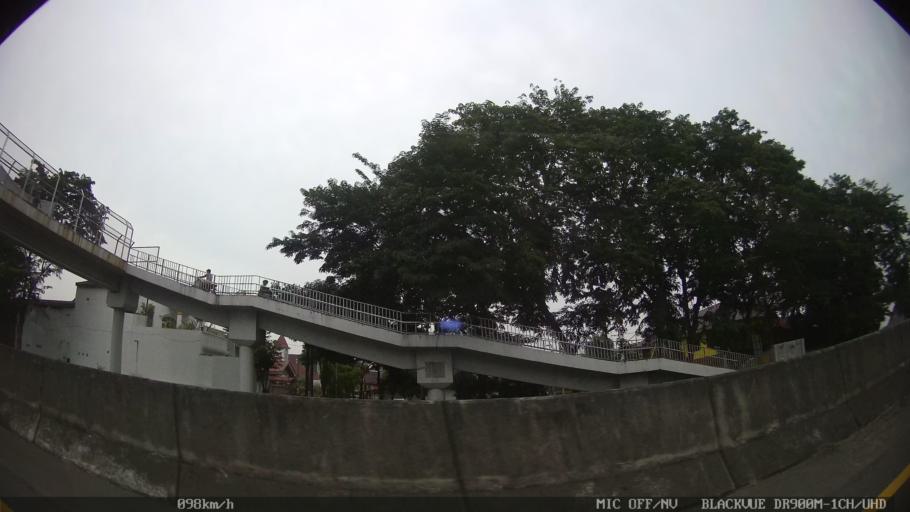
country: ID
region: North Sumatra
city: Medan
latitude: 3.5685
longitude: 98.7258
